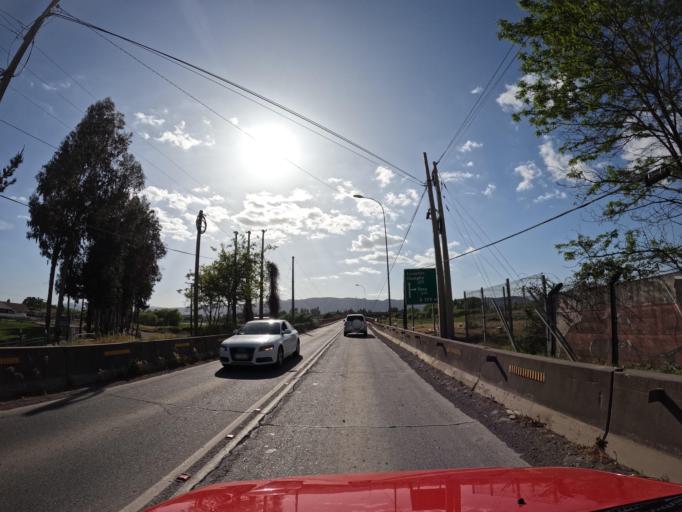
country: CL
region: Maule
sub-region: Provincia de Curico
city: Rauco
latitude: -34.9352
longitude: -71.2721
